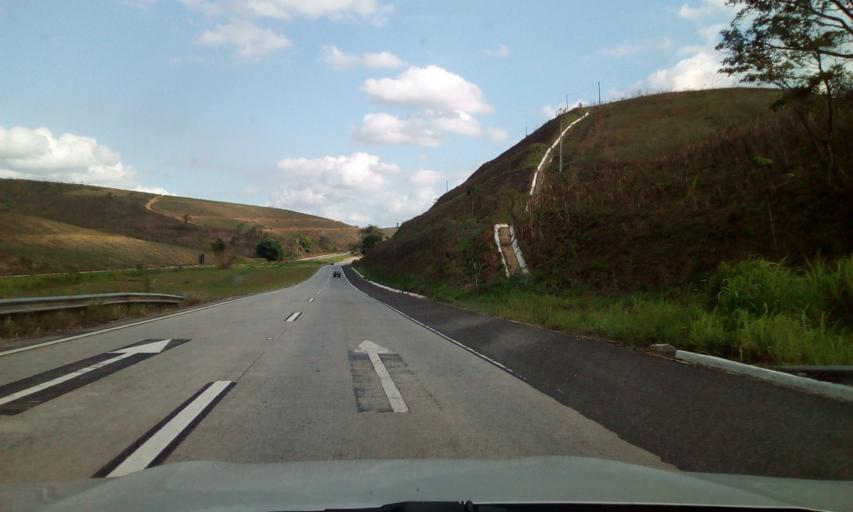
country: BR
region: Pernambuco
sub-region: Gameleira
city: Gameleira
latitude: -8.5546
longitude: -35.4333
